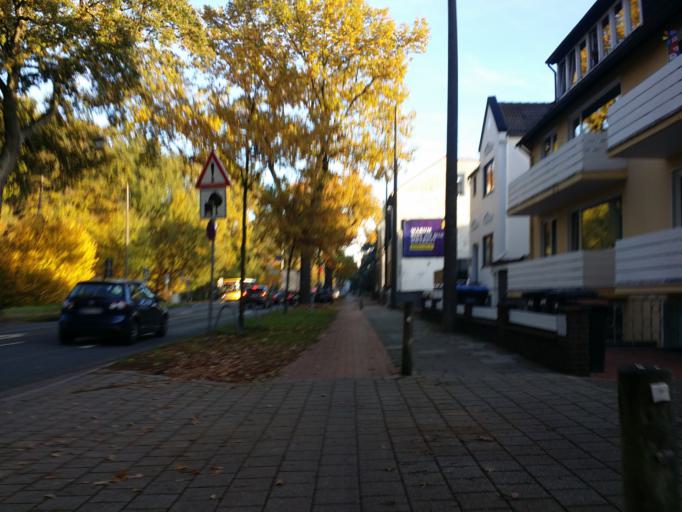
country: DE
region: Bremen
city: Bremen
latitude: 53.0380
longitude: 8.8133
